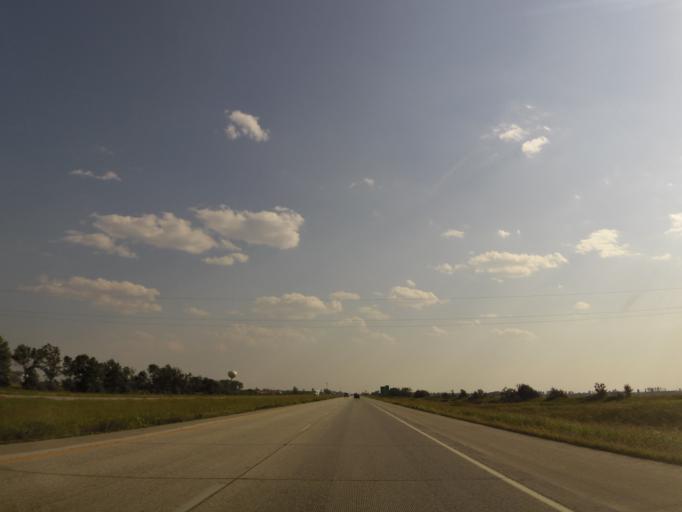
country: US
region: North Dakota
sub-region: Grand Forks County
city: Grand Forks
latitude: 47.9556
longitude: -97.0937
